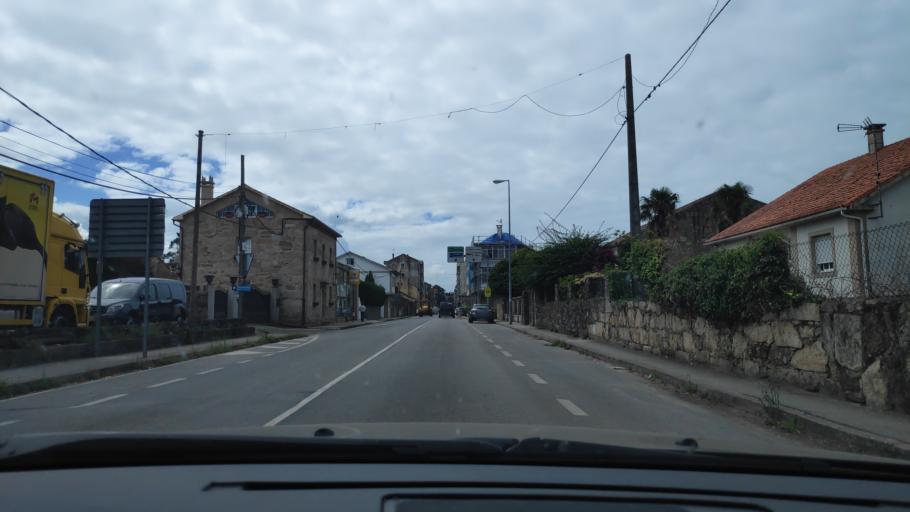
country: ES
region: Galicia
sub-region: Provincia de Pontevedra
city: Cambados
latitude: 42.5247
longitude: -8.8121
